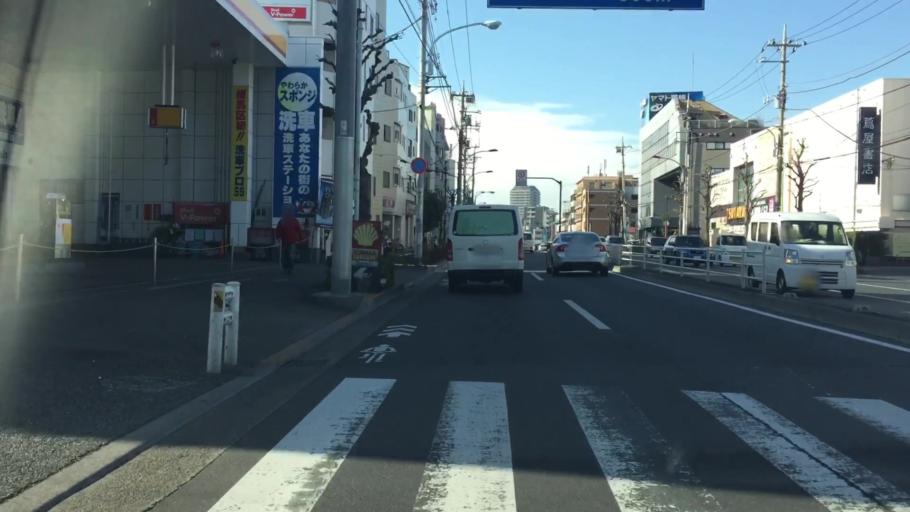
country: JP
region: Saitama
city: Wako
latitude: 35.7561
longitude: 139.6492
